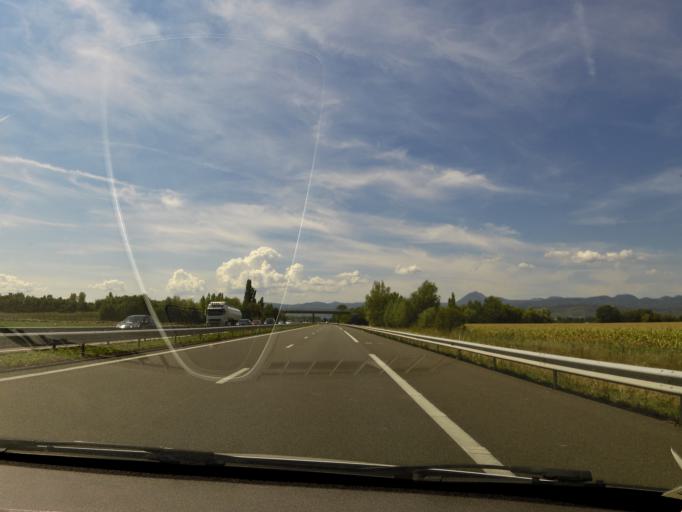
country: FR
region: Auvergne
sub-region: Departement du Puy-de-Dome
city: Malintrat
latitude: 45.8169
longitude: 3.1772
